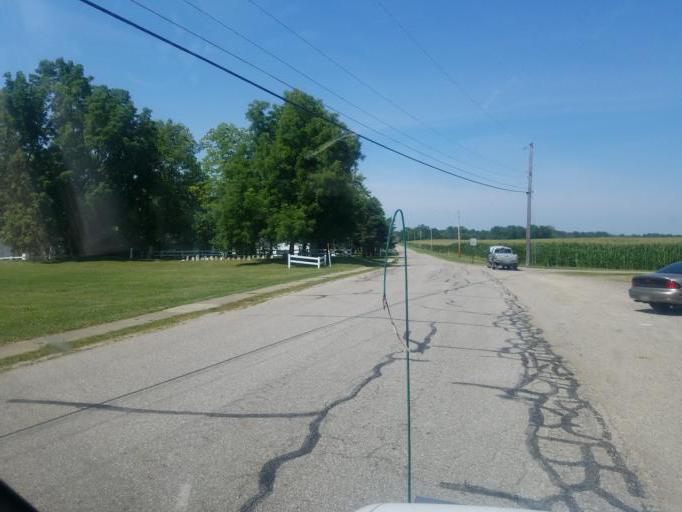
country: US
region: Ohio
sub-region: Champaign County
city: North Lewisburg
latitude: 40.2279
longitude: -83.5590
